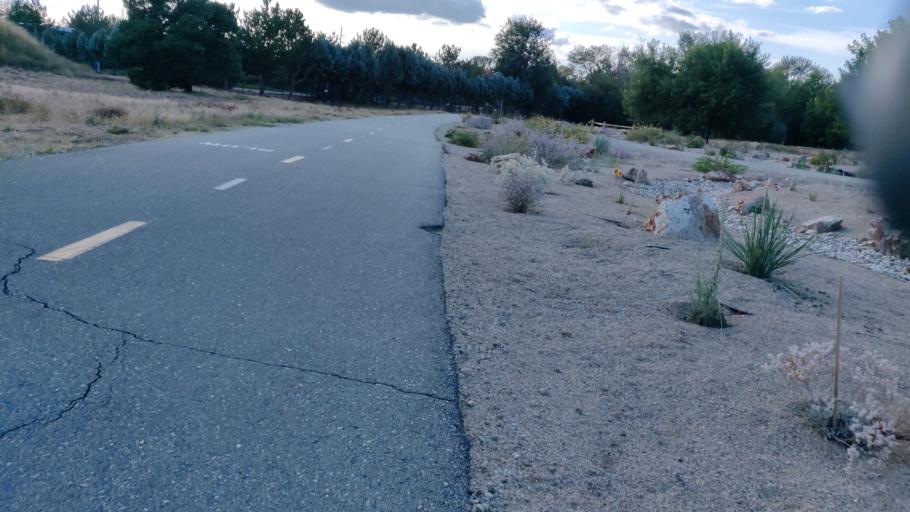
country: US
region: Idaho
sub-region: Ada County
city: Boise
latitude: 43.6006
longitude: -116.1738
